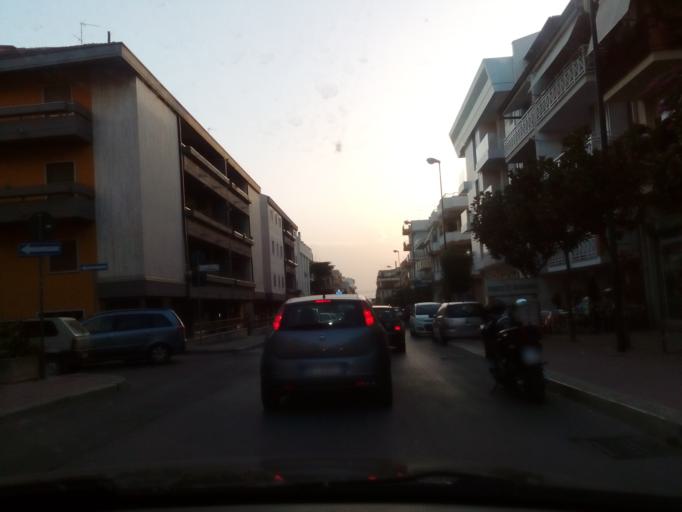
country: IT
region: Apulia
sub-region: Provincia di Bari
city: Gravina in Puglia
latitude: 40.8177
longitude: 16.4283
